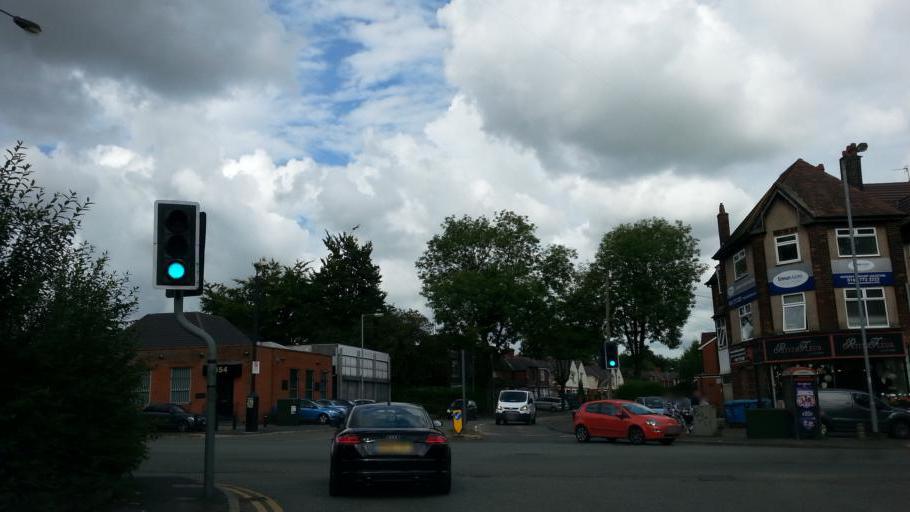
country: GB
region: England
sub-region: Borough of Bury
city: Prestwich
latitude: 53.5368
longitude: -2.2747
